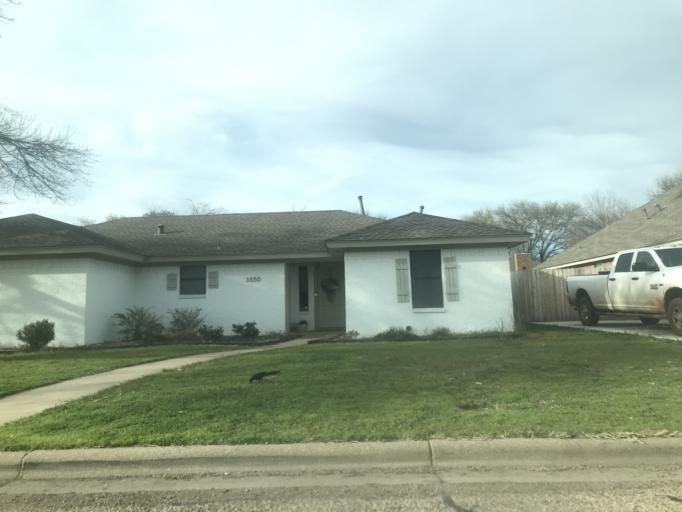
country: US
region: Texas
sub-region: Taylor County
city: Abilene
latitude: 32.3967
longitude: -99.7694
